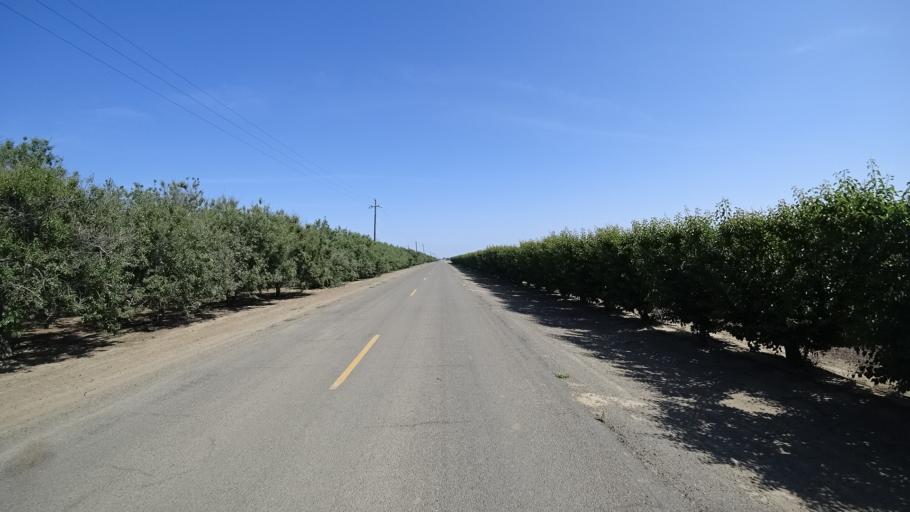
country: US
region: California
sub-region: Kings County
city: Kettleman City
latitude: 36.0631
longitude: -120.0036
